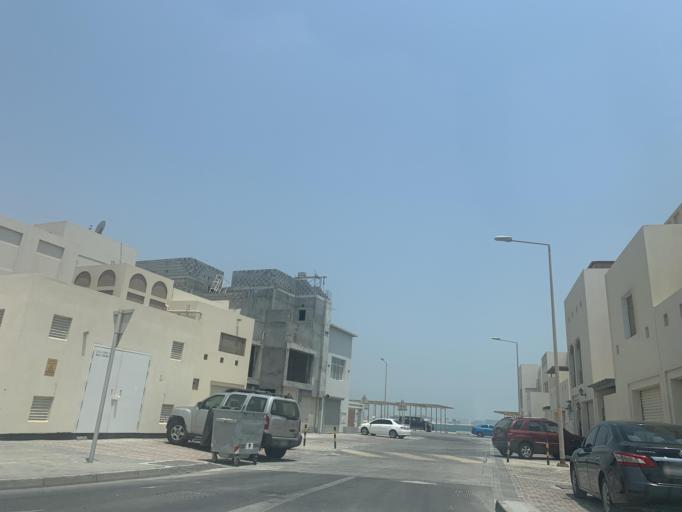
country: BH
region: Muharraq
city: Al Hadd
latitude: 26.2347
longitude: 50.6793
